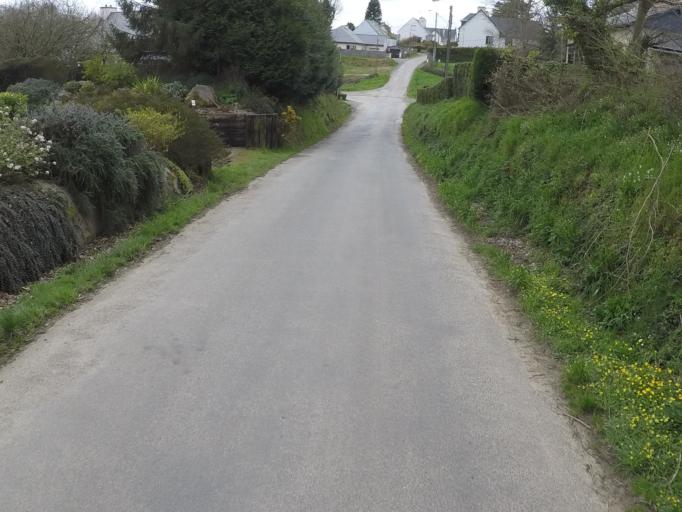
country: FR
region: Brittany
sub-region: Departement des Cotes-d'Armor
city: Plouha
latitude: 48.6722
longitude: -2.9203
